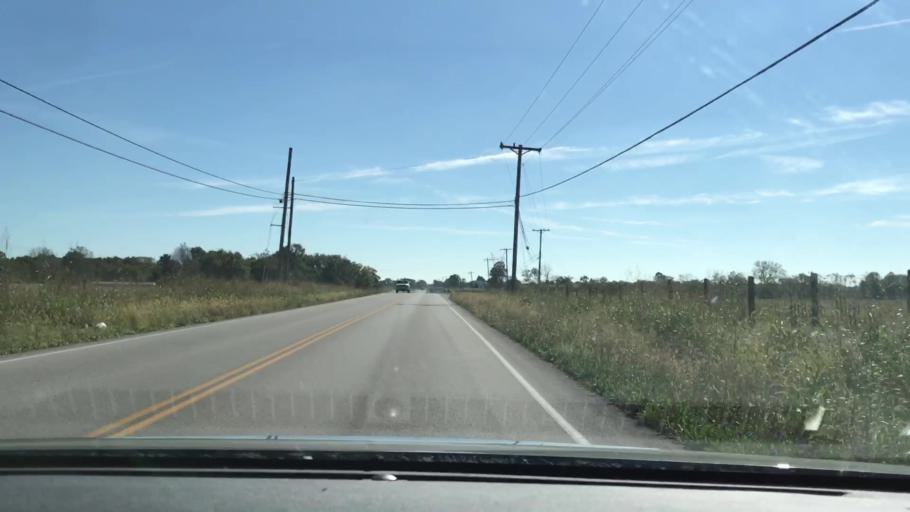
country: US
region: Kentucky
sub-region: Christian County
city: Hopkinsville
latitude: 36.8599
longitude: -87.4323
